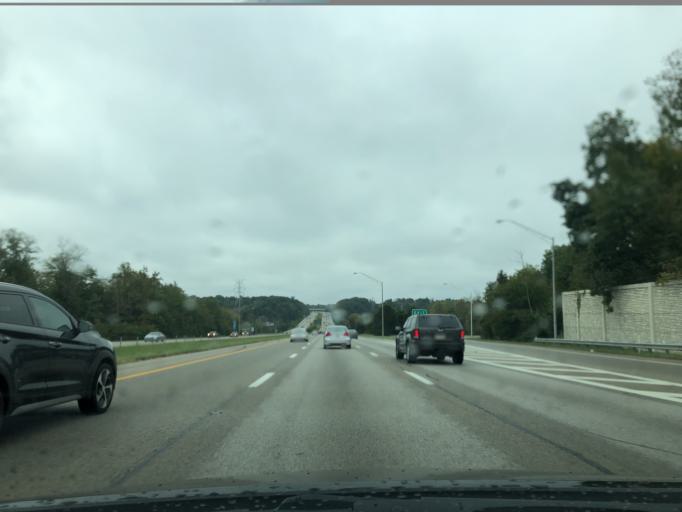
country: US
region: Ohio
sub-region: Hamilton County
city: The Village of Indian Hill
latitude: 39.2451
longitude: -84.3033
